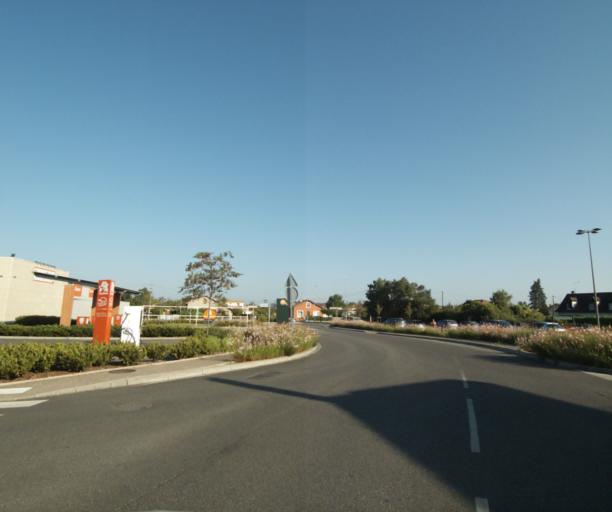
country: FR
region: Midi-Pyrenees
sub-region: Departement du Tarn-et-Garonne
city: Montauban
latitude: 44.0313
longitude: 1.3679
